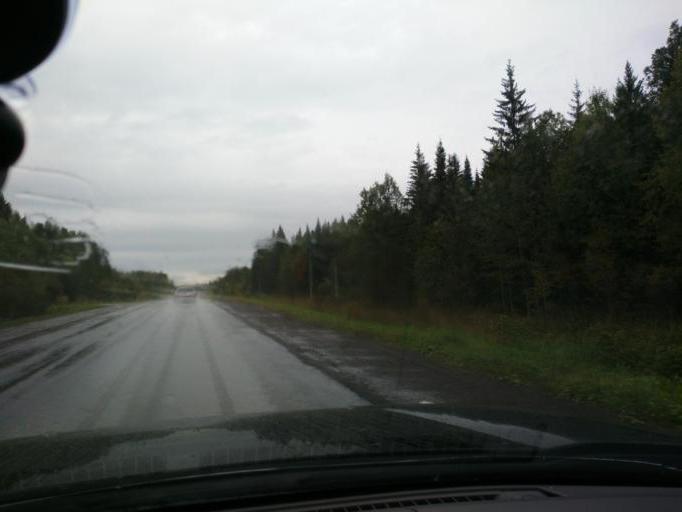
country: RU
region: Perm
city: Kultayevo
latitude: 57.8200
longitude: 55.8016
